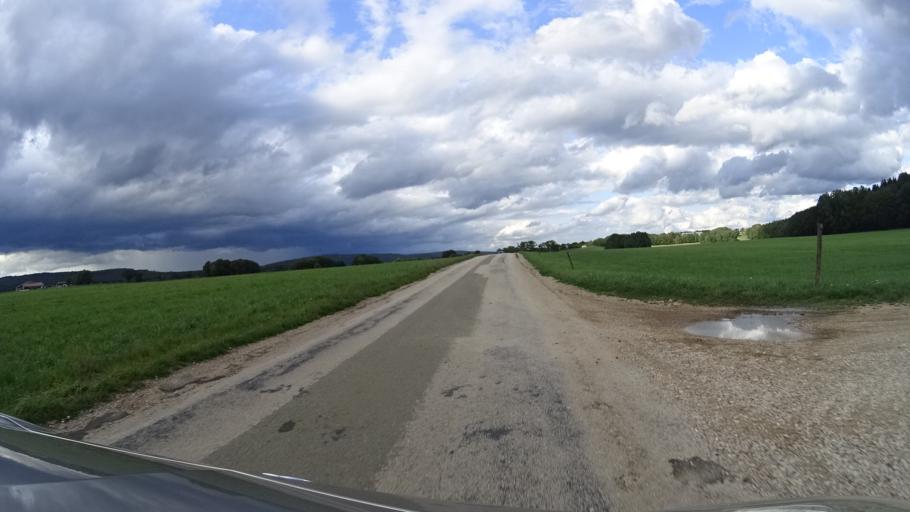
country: FR
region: Franche-Comte
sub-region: Departement du Doubs
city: Nancray
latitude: 47.2335
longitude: 6.1658
